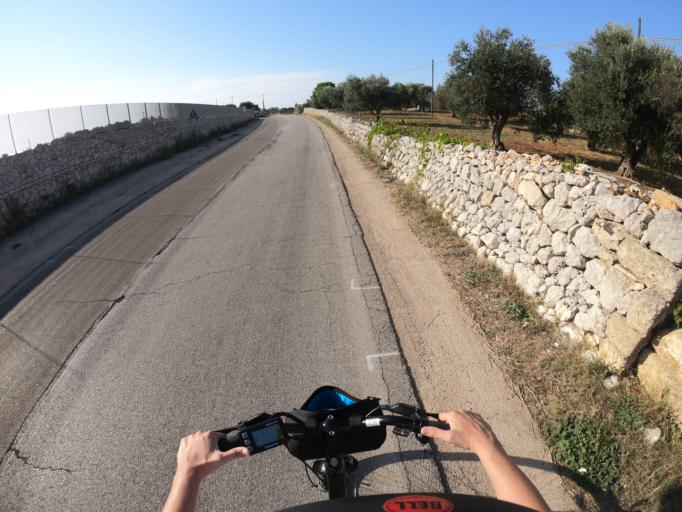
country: IT
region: Apulia
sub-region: Provincia di Lecce
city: Castrignano del Capo
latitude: 39.8203
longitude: 18.3558
